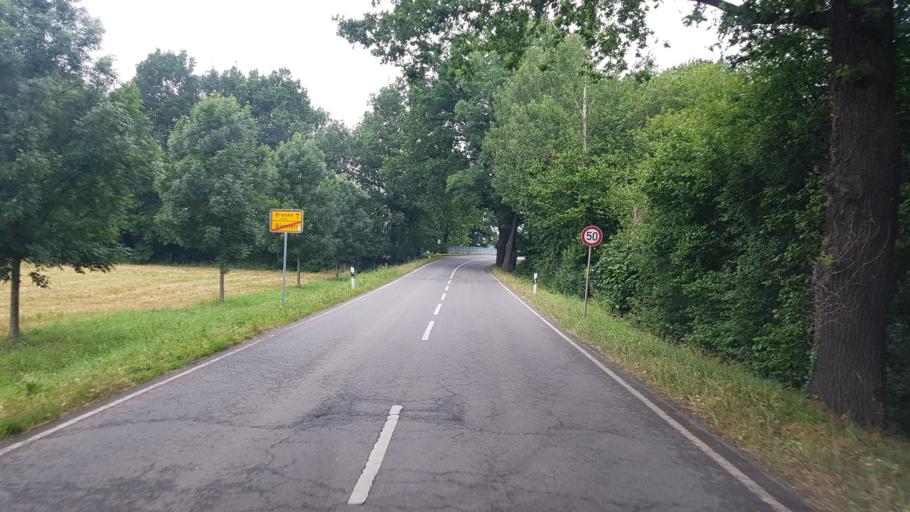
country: DE
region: Brandenburg
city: Schwarzbach
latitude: 51.4762
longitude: 13.9384
